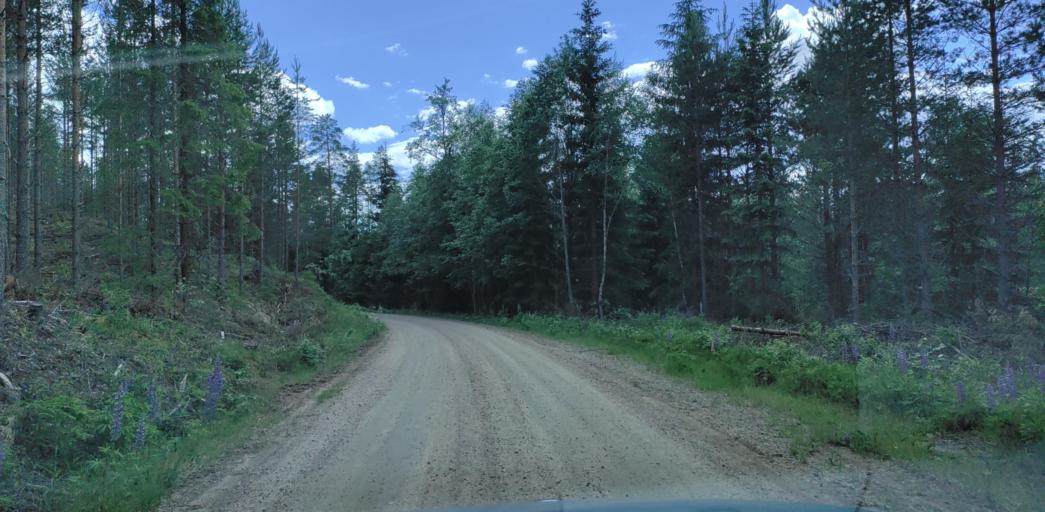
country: SE
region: Vaermland
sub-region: Hagfors Kommun
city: Ekshaerad
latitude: 60.0758
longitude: 13.2913
